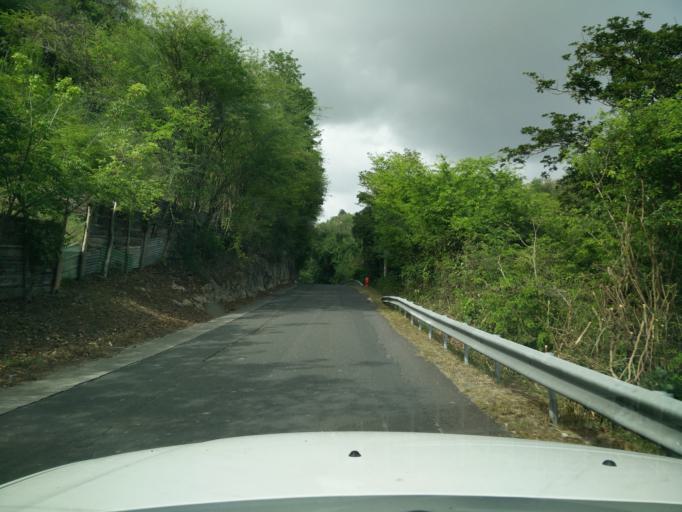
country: GP
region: Guadeloupe
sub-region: Guadeloupe
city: Le Gosier
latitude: 16.2204
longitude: -61.4751
